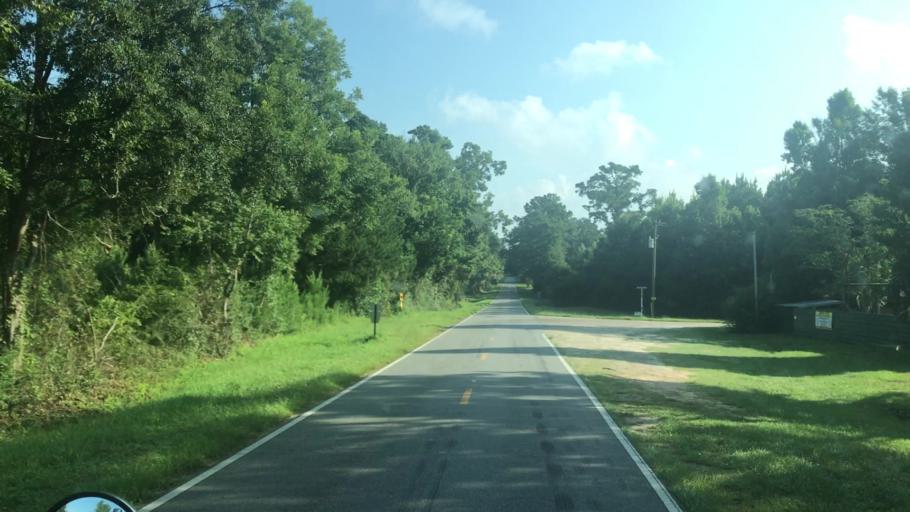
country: US
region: Florida
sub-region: Gadsden County
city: Quincy
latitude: 30.6880
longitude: -84.5390
